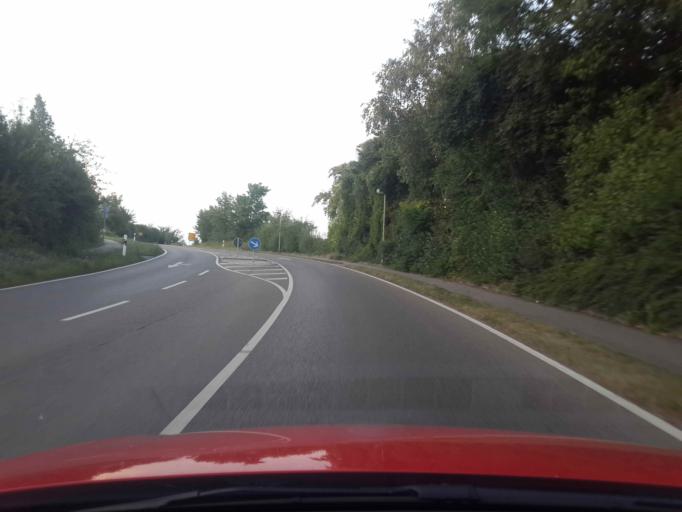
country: DE
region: Baden-Wuerttemberg
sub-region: Regierungsbezirk Stuttgart
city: Nordheim
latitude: 49.1114
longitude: 9.1285
